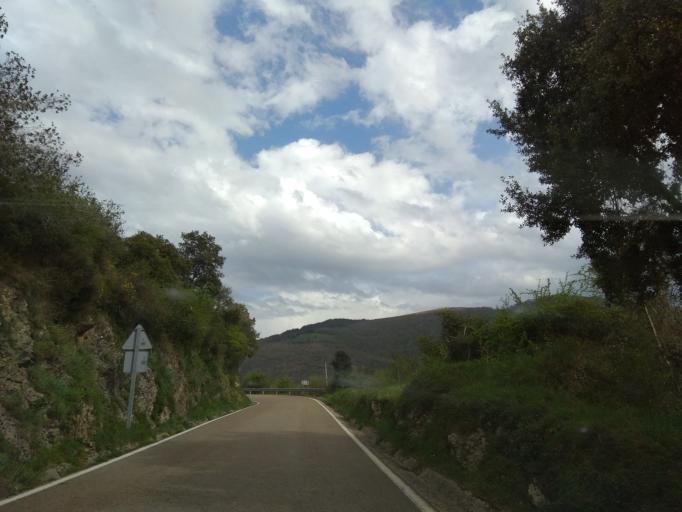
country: ES
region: Cantabria
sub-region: Provincia de Cantabria
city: San Vicente de la Barquera
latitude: 43.2537
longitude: -4.4702
